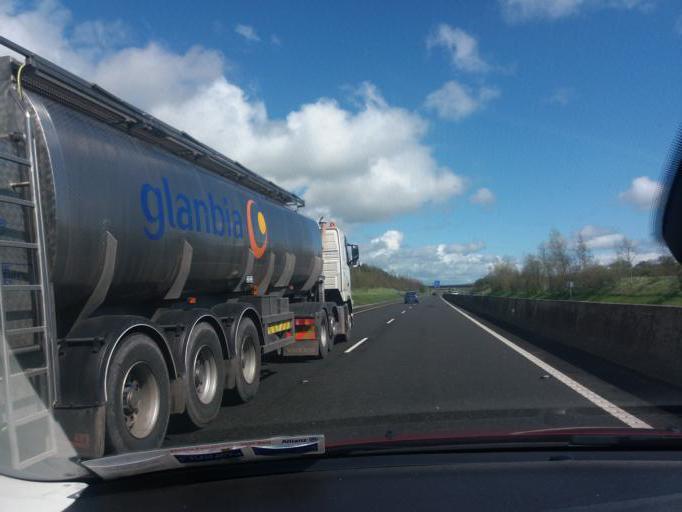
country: IE
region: Leinster
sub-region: Laois
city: Rathdowney
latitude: 52.7229
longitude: -7.5946
